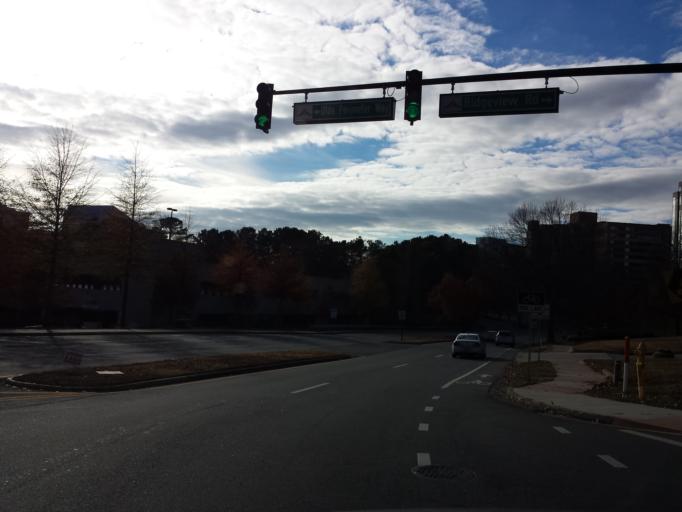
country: US
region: Georgia
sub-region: DeKalb County
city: Dunwoody
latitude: 33.9309
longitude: -84.3439
